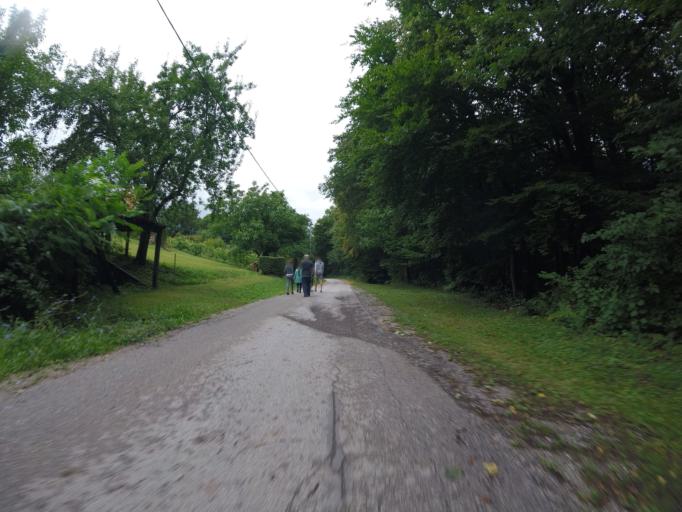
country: HR
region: Zagrebacka
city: Mraclin
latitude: 45.5972
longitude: 16.0796
